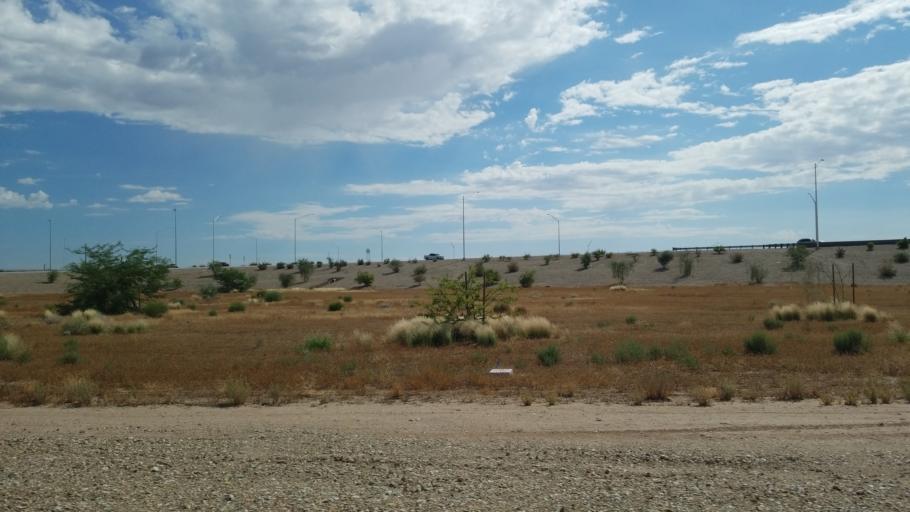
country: US
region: Arizona
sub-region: Maricopa County
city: Citrus Park
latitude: 33.5597
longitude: -112.4200
